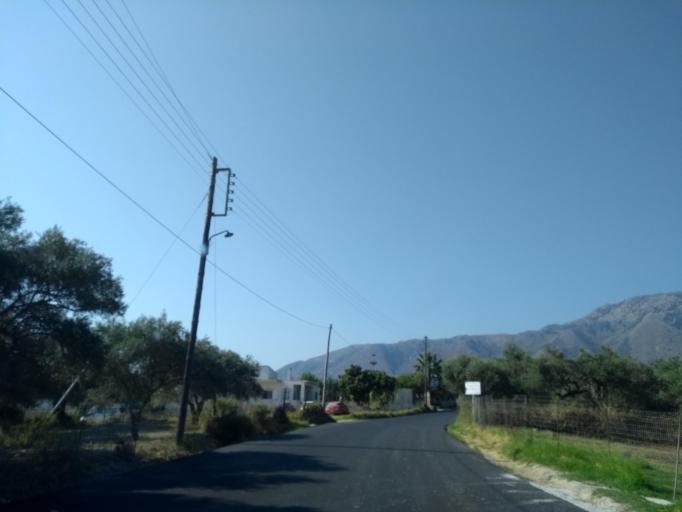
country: GR
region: Crete
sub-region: Nomos Chanias
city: Georgioupolis
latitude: 35.3376
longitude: 24.3020
